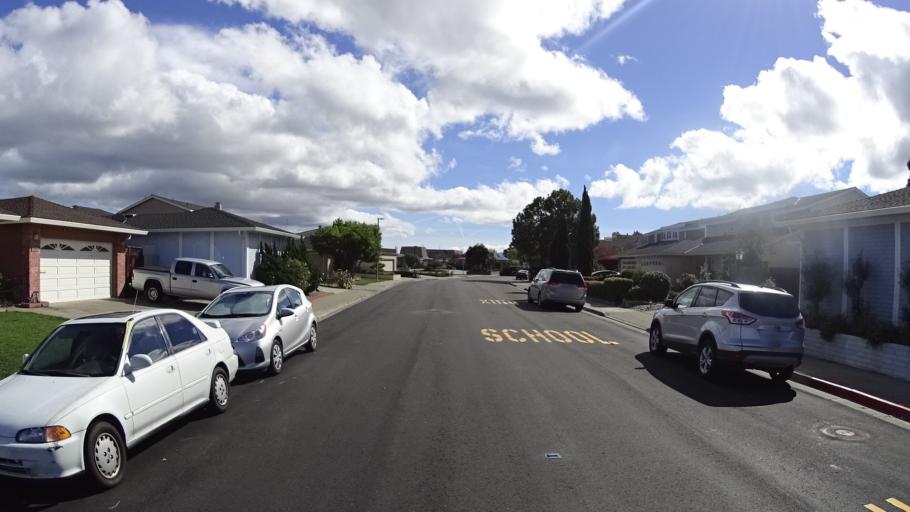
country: US
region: California
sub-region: San Mateo County
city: Foster City
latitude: 37.5613
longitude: -122.2500
